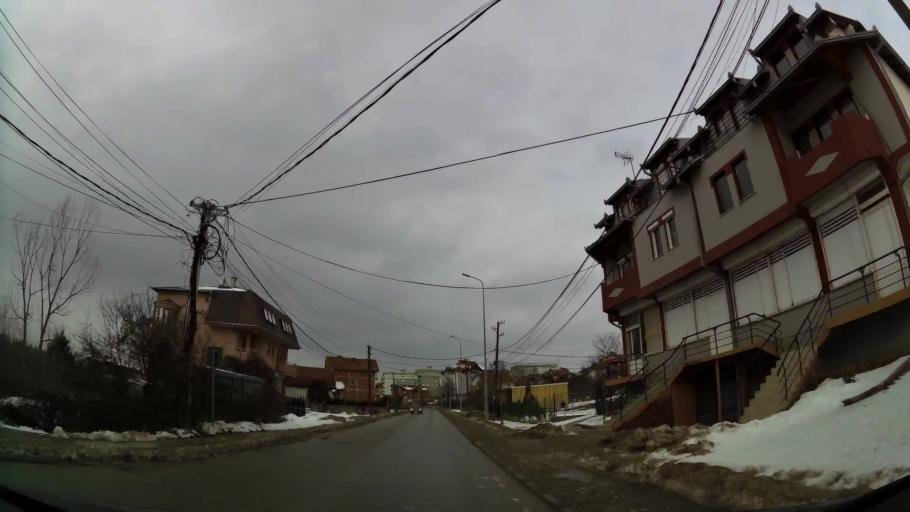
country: XK
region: Pristina
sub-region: Komuna e Prishtines
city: Pristina
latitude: 42.6504
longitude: 21.1938
